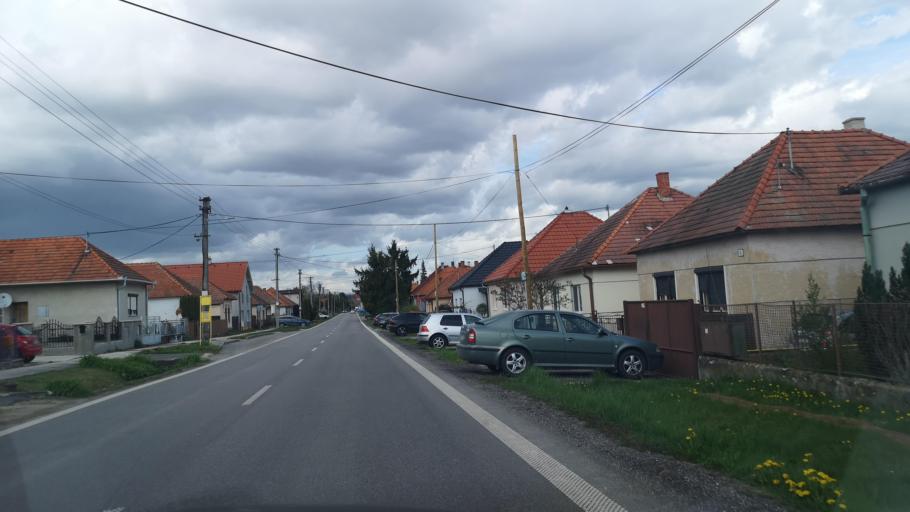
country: SK
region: Nitriansky
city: Zlate Moravce
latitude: 48.3294
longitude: 18.3509
